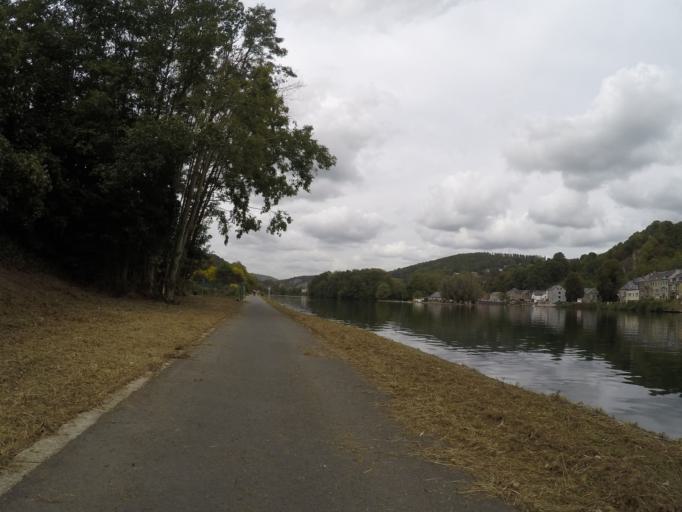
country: BE
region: Wallonia
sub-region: Province de Namur
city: Anhee
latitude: 50.3190
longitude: 4.8759
